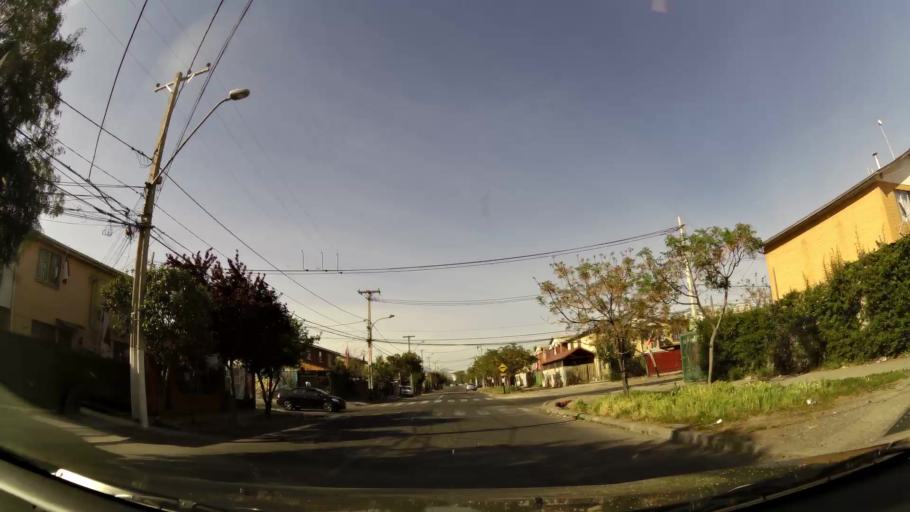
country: CL
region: Santiago Metropolitan
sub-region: Provincia de Cordillera
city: Puente Alto
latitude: -33.6104
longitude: -70.5967
